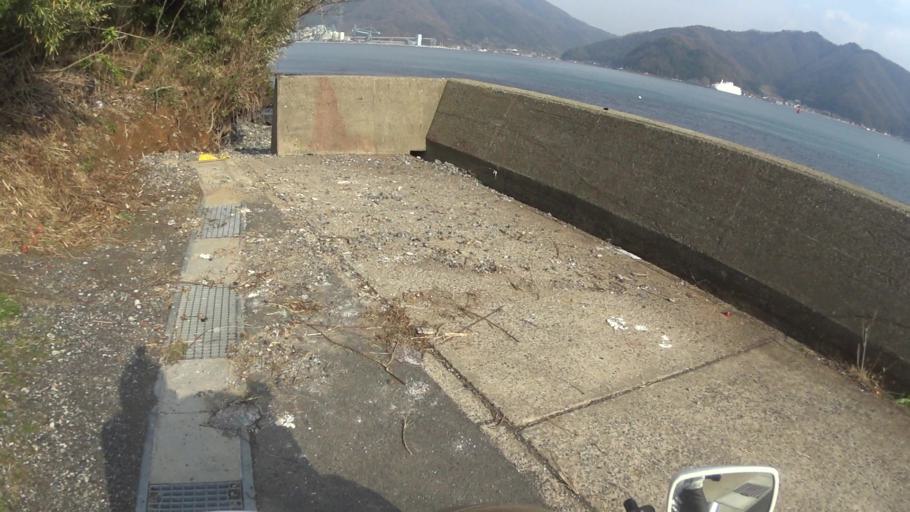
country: JP
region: Kyoto
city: Maizuru
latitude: 35.5115
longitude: 135.3321
